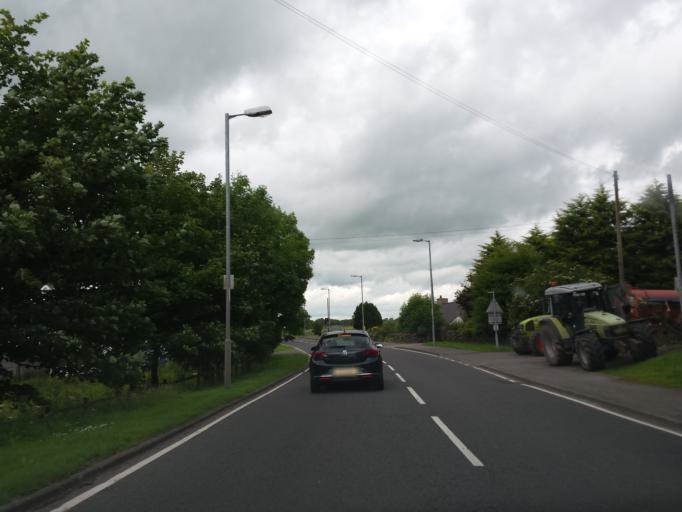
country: GB
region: Scotland
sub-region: Dumfries and Galloway
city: Dalbeattie
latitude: 55.0156
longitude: -3.8628
